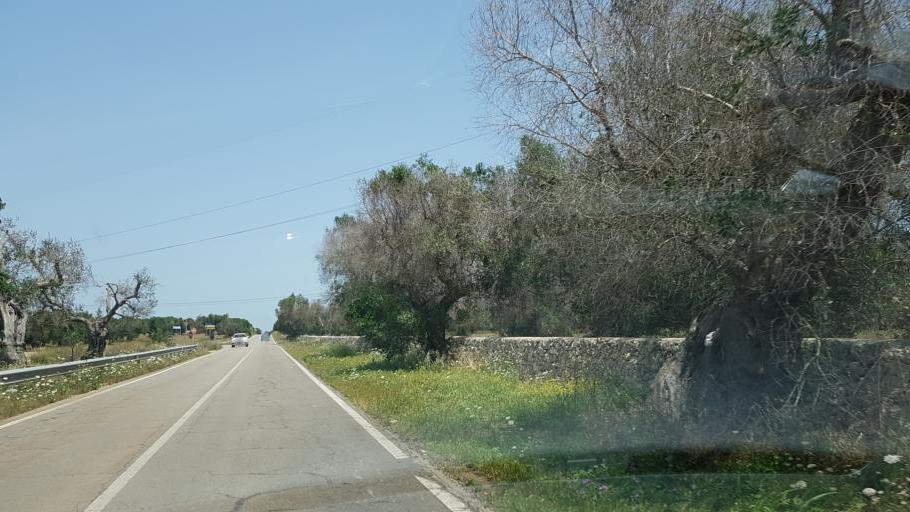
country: IT
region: Apulia
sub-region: Provincia di Lecce
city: Porto Cesareo
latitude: 40.2887
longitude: 17.9120
